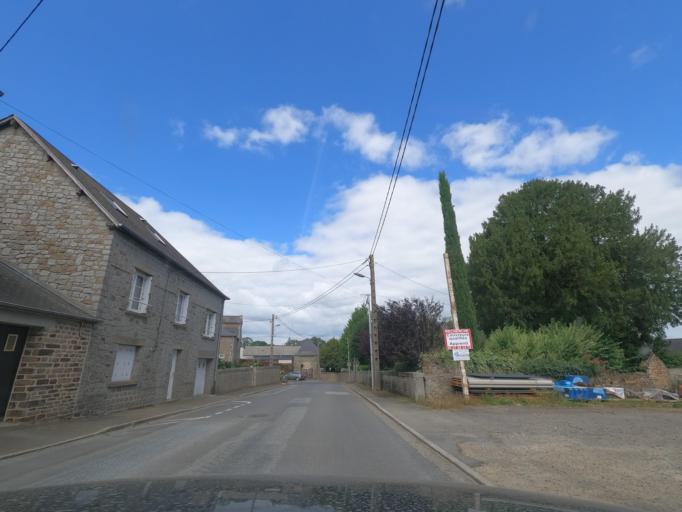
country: FR
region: Pays de la Loire
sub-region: Departement de la Mayenne
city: Fougerolles-du-Plessis
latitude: 48.4760
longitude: -0.9716
